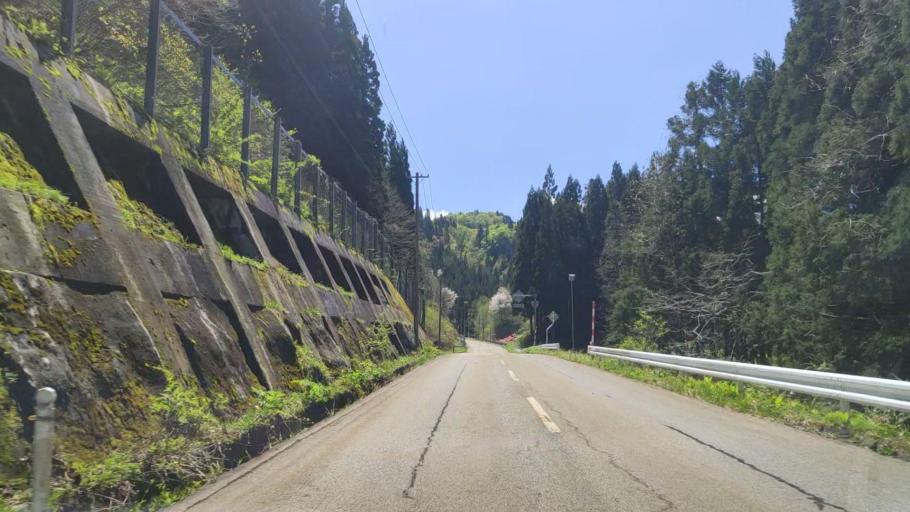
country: JP
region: Yamagata
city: Shinjo
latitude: 38.9692
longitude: 140.3537
